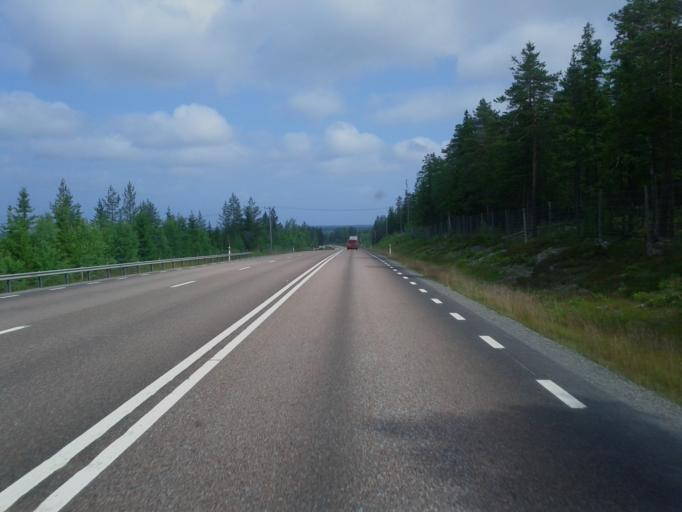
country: SE
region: Vaesterbotten
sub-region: Skelleftea Kommun
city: Burea
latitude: 64.4548
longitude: 21.2864
